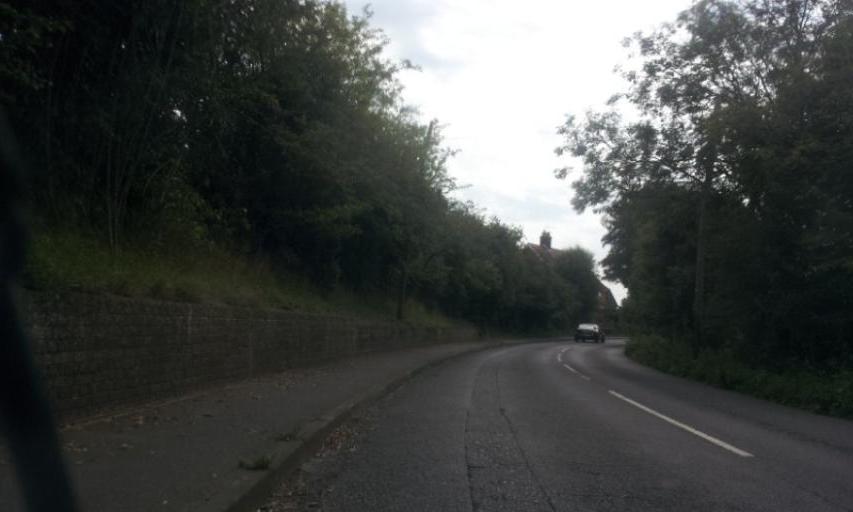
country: GB
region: England
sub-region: Kent
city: Yalding
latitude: 51.2177
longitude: 0.4208
